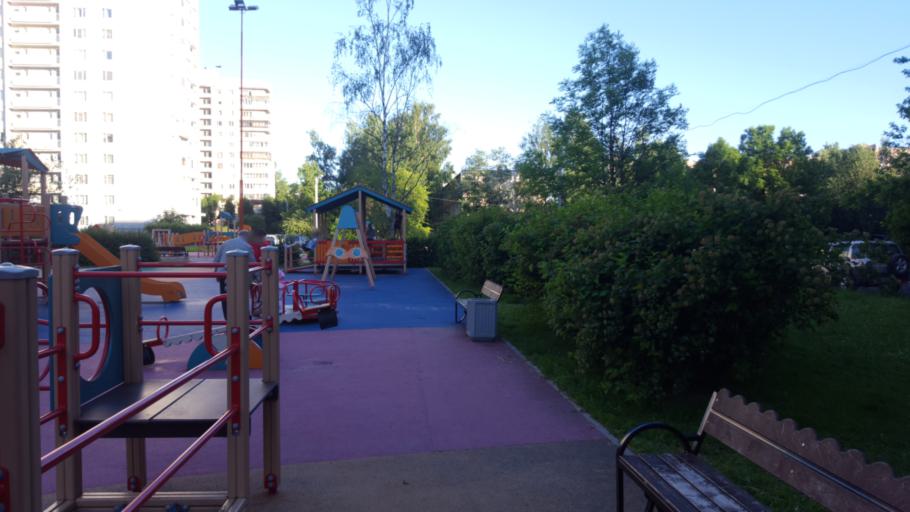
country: RU
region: St.-Petersburg
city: Krasnogvargeisky
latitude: 59.9153
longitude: 30.4924
